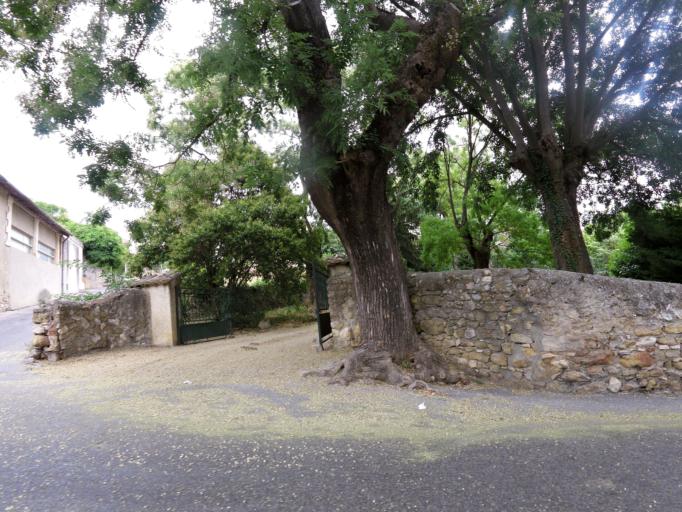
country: FR
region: Languedoc-Roussillon
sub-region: Departement du Gard
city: Saint-Genies-de-Malgoires
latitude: 43.9622
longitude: 4.2106
